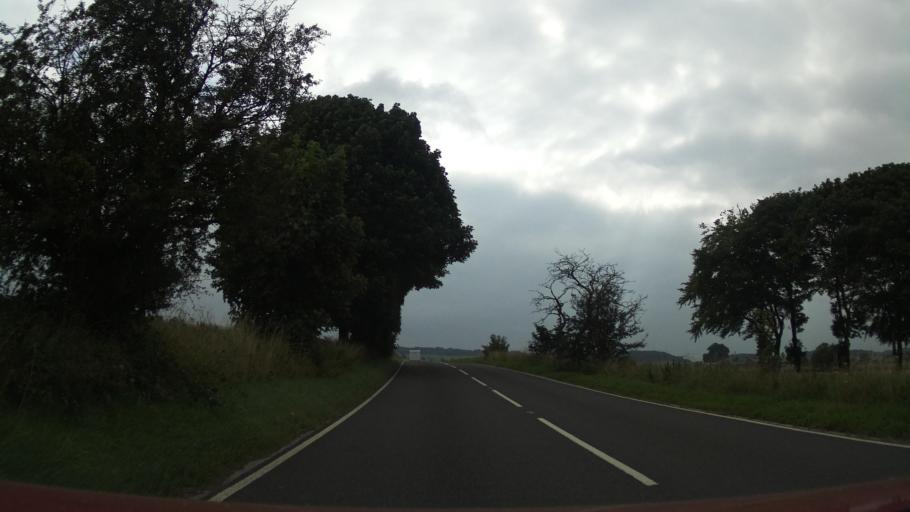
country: GB
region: England
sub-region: Staffordshire
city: Mayfield
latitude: 53.0318
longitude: -1.8335
